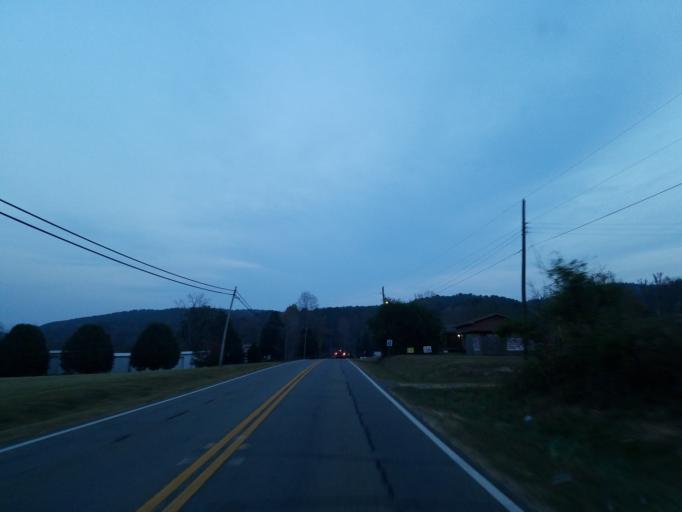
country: US
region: Georgia
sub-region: Pickens County
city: Jasper
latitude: 34.5106
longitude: -84.5137
